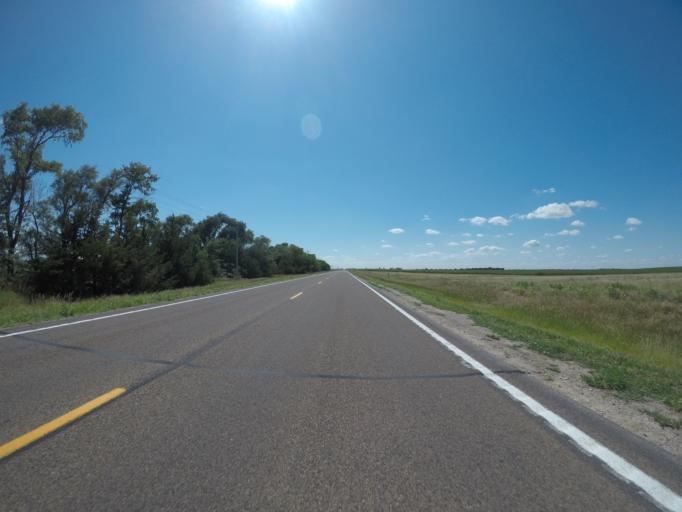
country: US
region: Nebraska
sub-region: Chase County
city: Imperial
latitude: 40.5376
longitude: -101.7315
